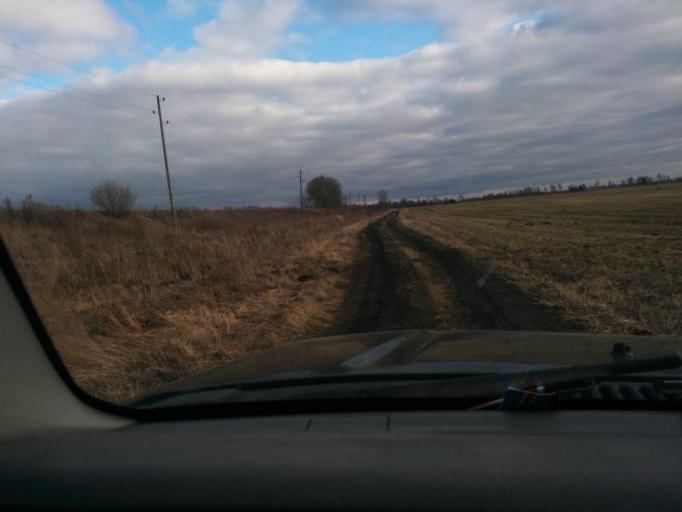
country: LV
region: Jelgava
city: Jelgava
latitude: 56.6905
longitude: 23.6868
